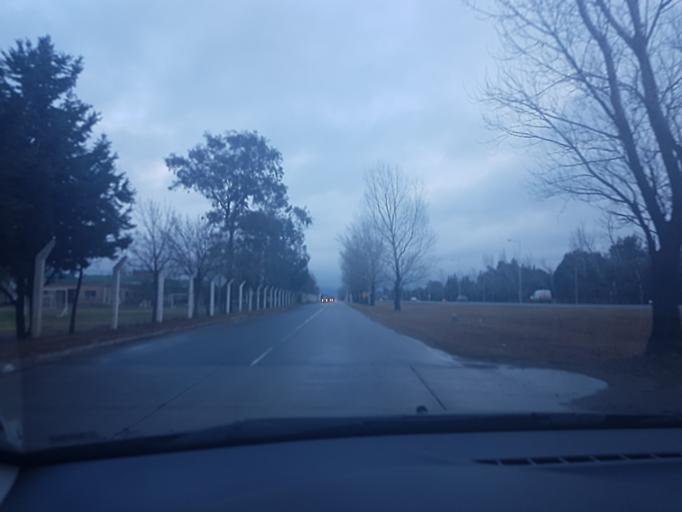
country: AR
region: Cordoba
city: Villa Allende
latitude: -31.3031
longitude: -64.2420
